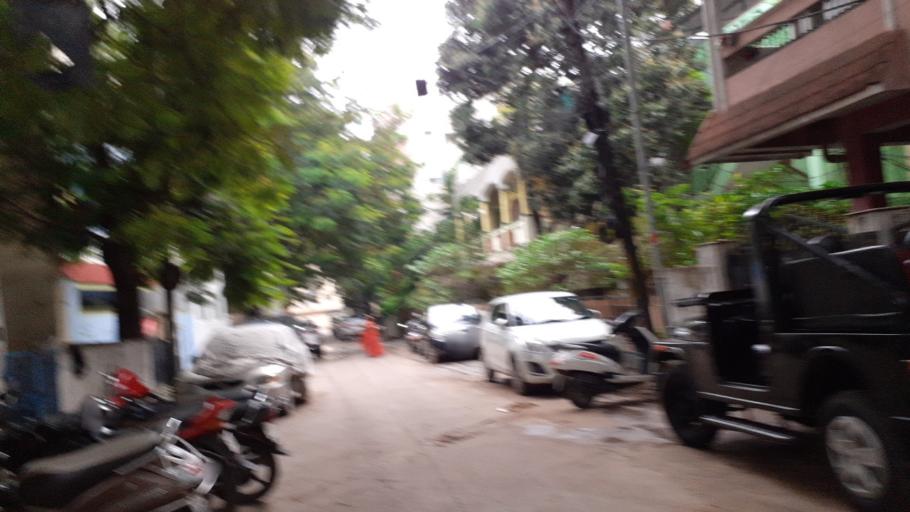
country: IN
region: Telangana
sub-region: Rangareddi
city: Kukatpalli
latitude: 17.4474
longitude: 78.4460
